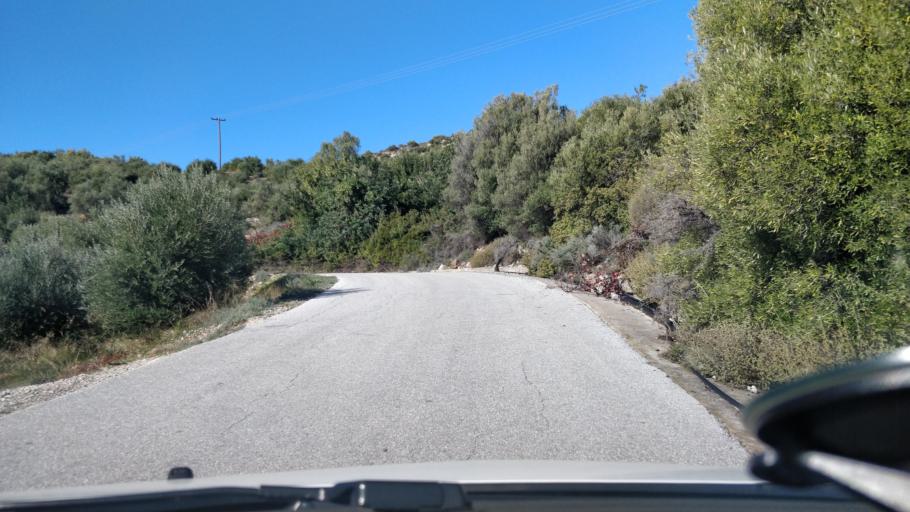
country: GR
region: Crete
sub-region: Nomos Lasithiou
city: Gra Liyia
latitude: 35.0188
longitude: 25.5509
